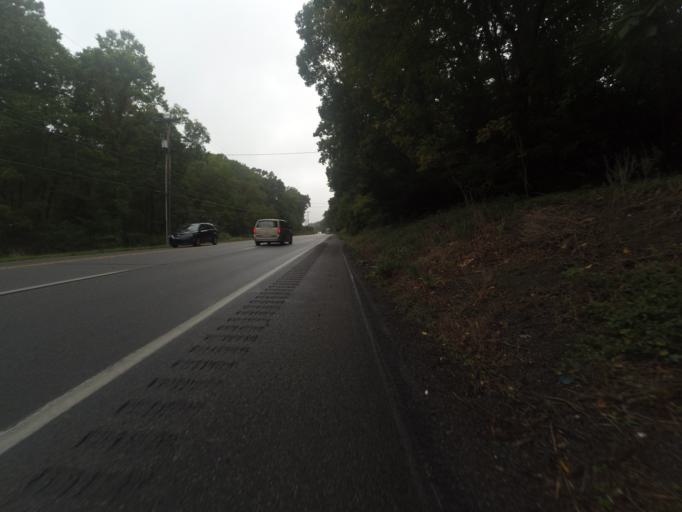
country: US
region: Pennsylvania
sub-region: Huntingdon County
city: Huntingdon
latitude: 40.4964
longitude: -78.0506
